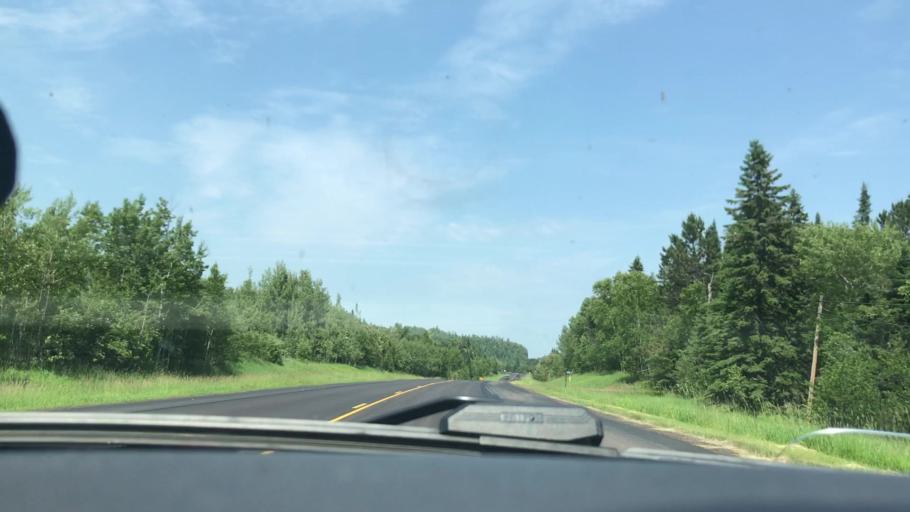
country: US
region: Minnesota
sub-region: Lake County
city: Silver Bay
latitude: 47.3555
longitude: -91.1806
